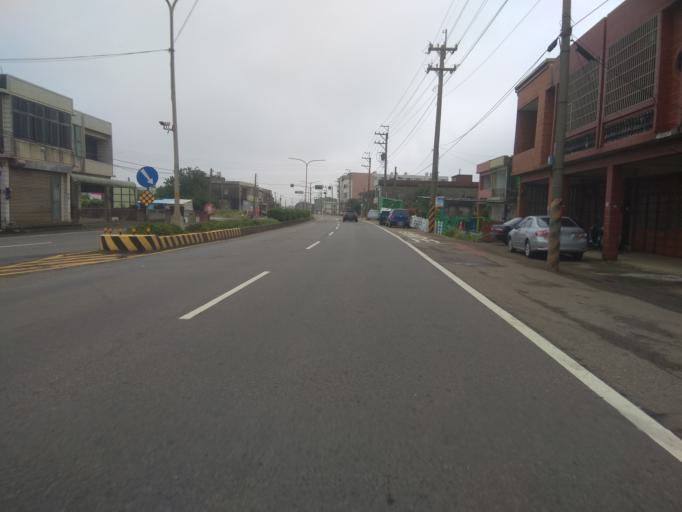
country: TW
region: Taiwan
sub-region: Hsinchu
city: Zhubei
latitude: 25.0015
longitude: 121.0377
